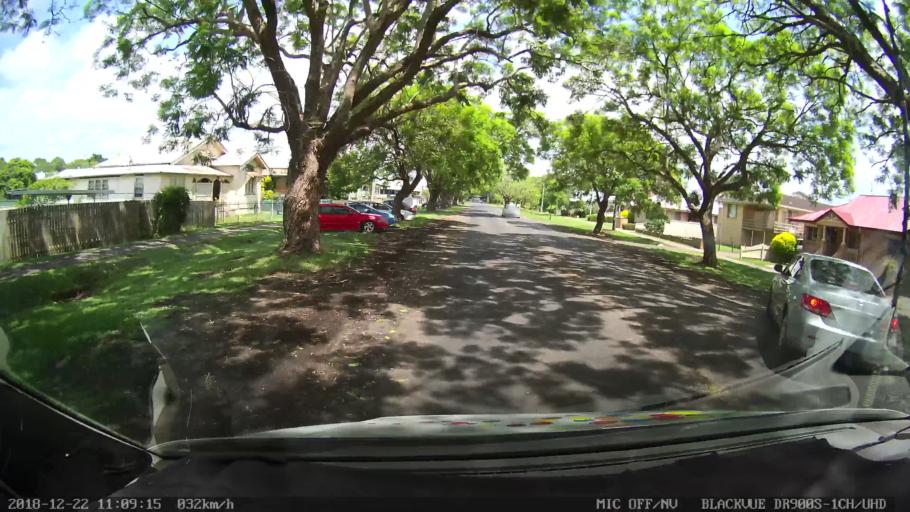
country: AU
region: New South Wales
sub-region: Clarence Valley
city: Grafton
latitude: -29.6865
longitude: 152.9299
